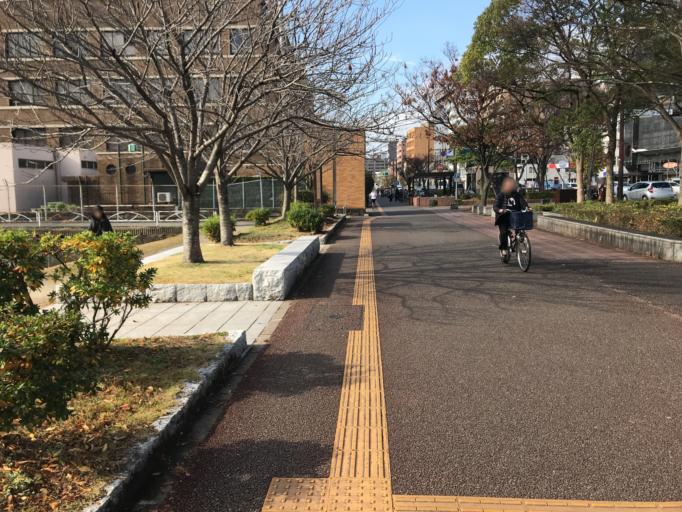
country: JP
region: Fukuoka
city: Fukuoka-shi
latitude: 33.5898
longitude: 130.3791
